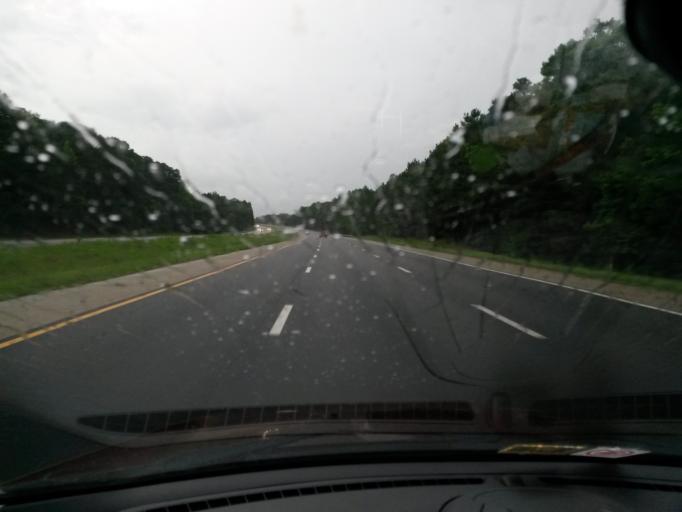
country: US
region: Virginia
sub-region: Chesterfield County
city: Enon
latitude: 37.4070
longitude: -77.3420
